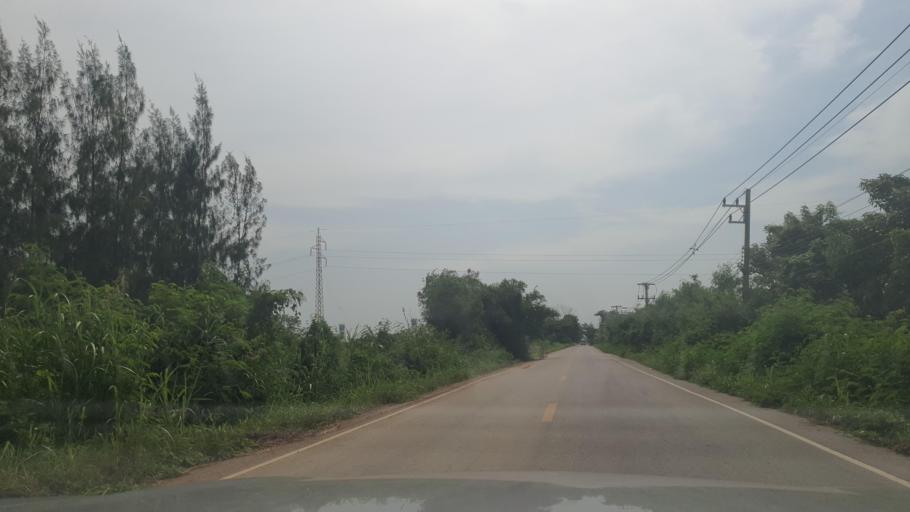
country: TH
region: Sukhothai
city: Si Samrong
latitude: 17.1182
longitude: 99.8714
